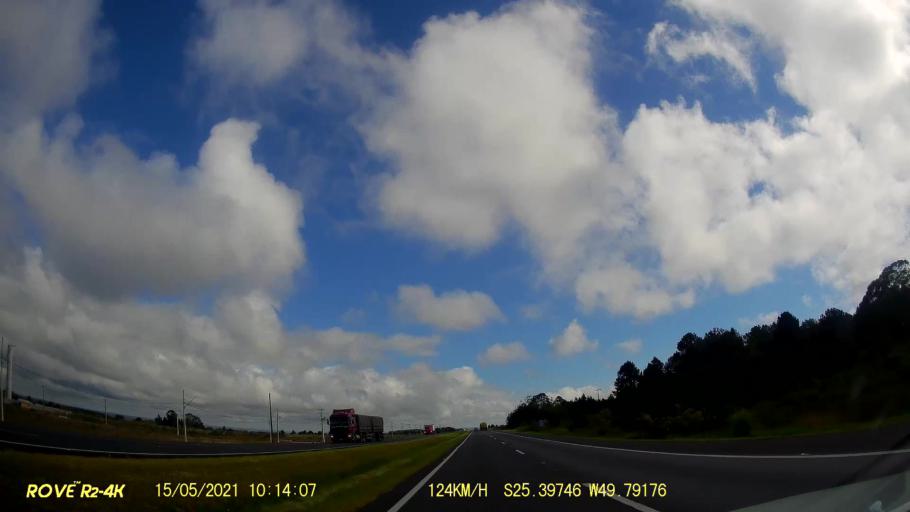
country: BR
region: Parana
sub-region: Palmeira
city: Palmeira
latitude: -25.3978
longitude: -49.7920
